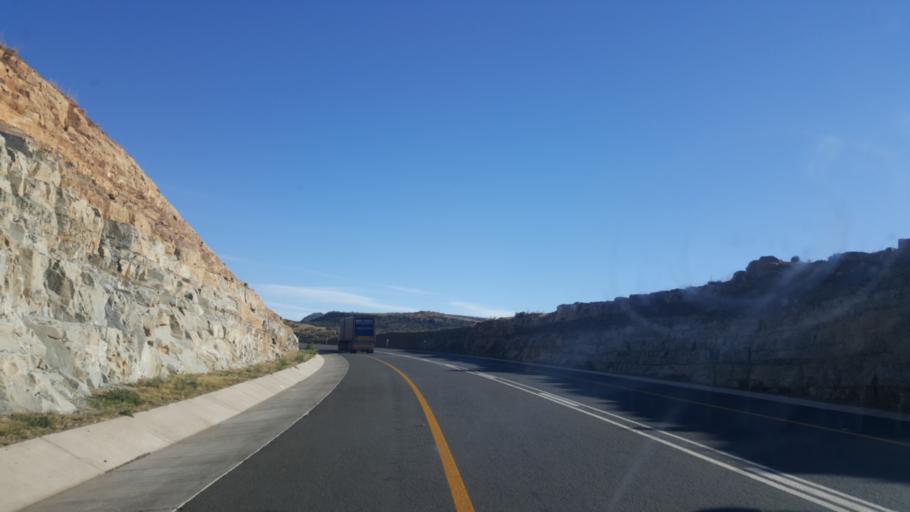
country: ZA
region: Eastern Cape
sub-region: Chris Hani District Municipality
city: Middelburg
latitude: -31.3784
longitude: 25.0344
